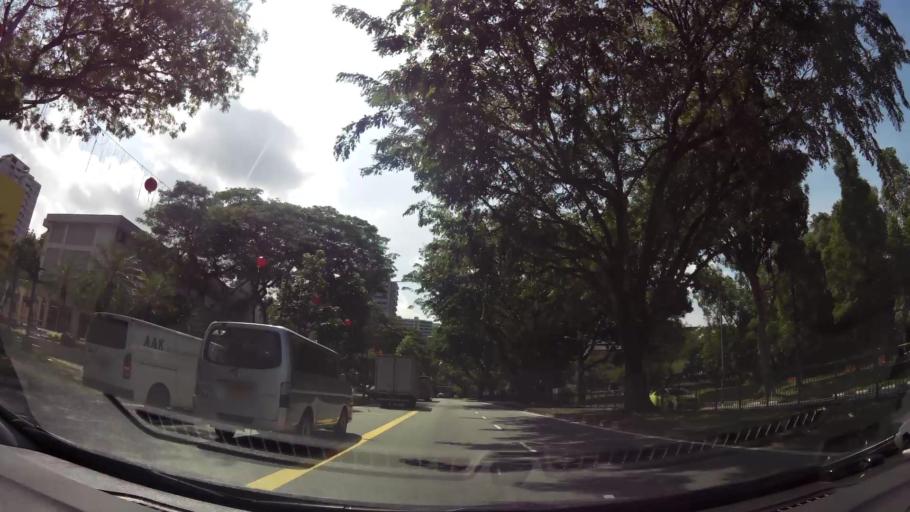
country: SG
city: Singapore
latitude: 1.3733
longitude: 103.8452
